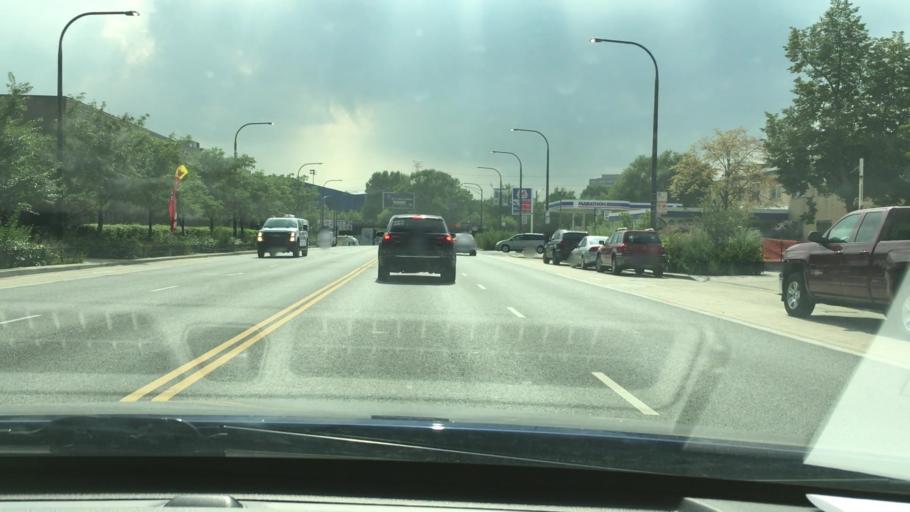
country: US
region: Illinois
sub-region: Cook County
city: Chicago
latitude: 41.8456
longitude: -87.6835
